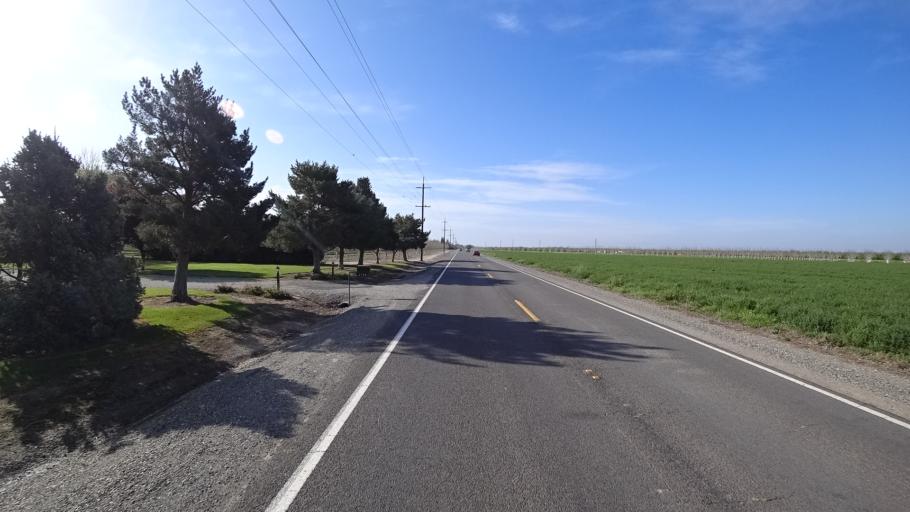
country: US
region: California
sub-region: Glenn County
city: Hamilton City
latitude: 39.6008
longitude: -122.0077
